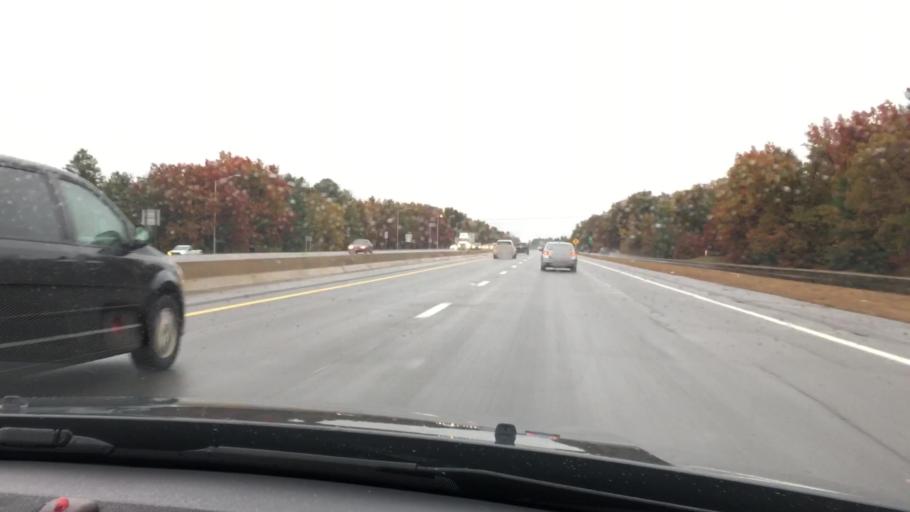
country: US
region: New Hampshire
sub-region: Hillsborough County
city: Litchfield
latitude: 42.8181
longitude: -71.4968
